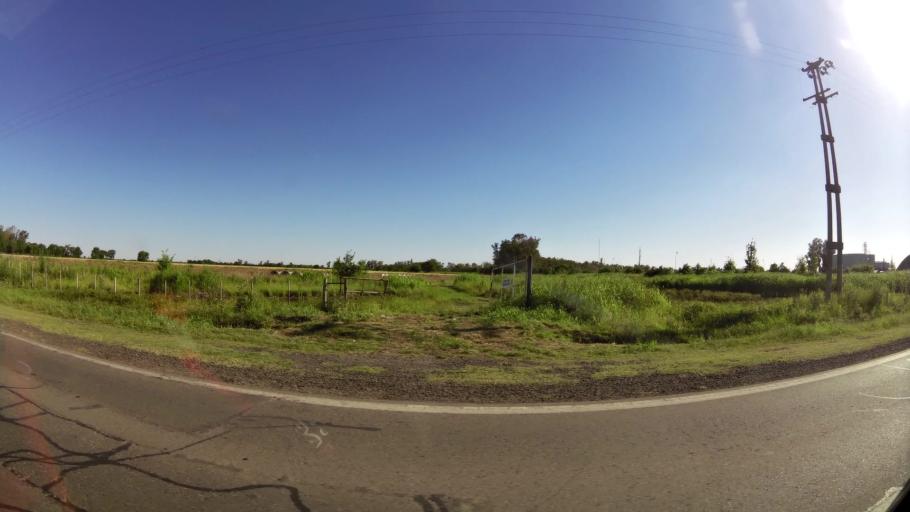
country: AR
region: Cordoba
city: San Francisco
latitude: -31.4247
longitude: -62.0495
